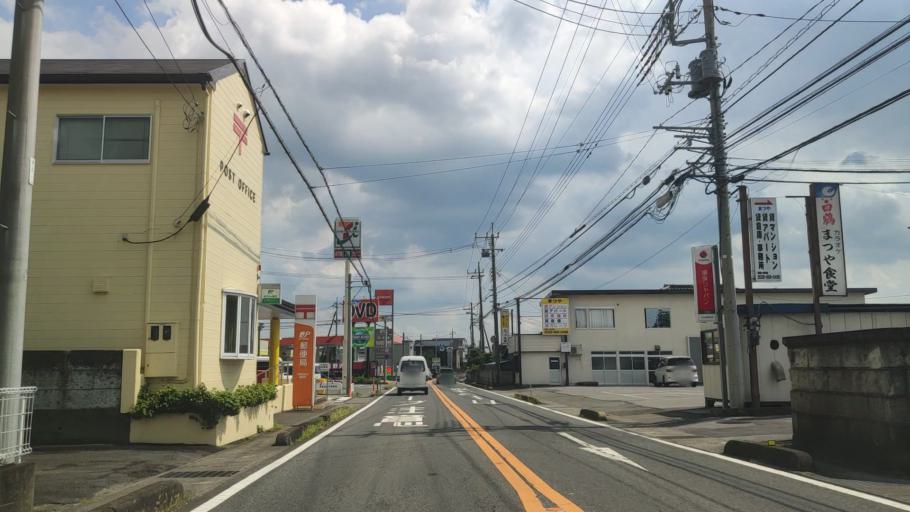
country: JP
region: Tochigi
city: Utsunomiya-shi
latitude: 36.6107
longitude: 139.8561
